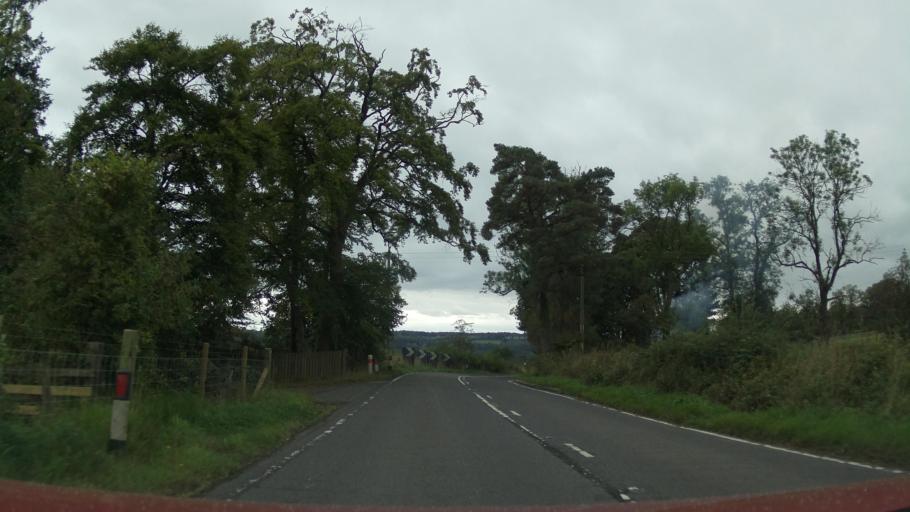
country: GB
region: Scotland
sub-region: Clackmannanshire
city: Dollar
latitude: 56.1703
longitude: -3.6391
